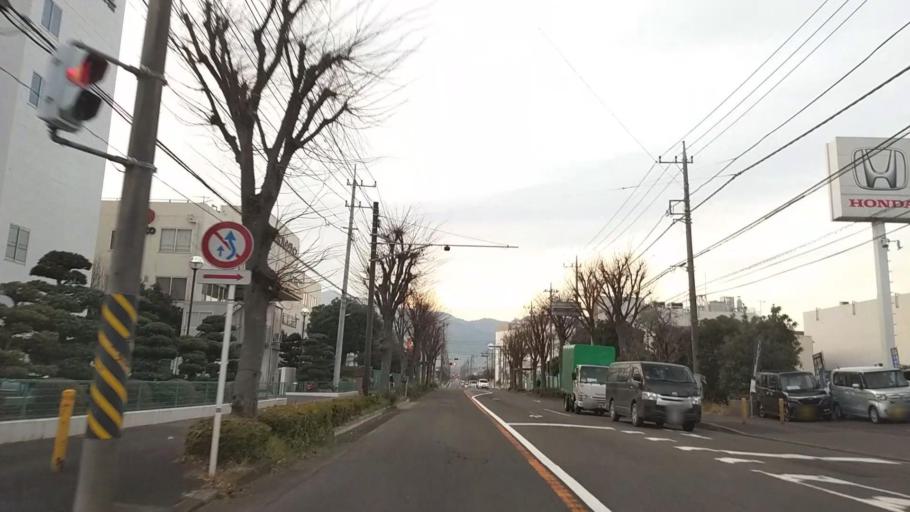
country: JP
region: Kanagawa
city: Atsugi
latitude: 35.4284
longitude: 139.3388
